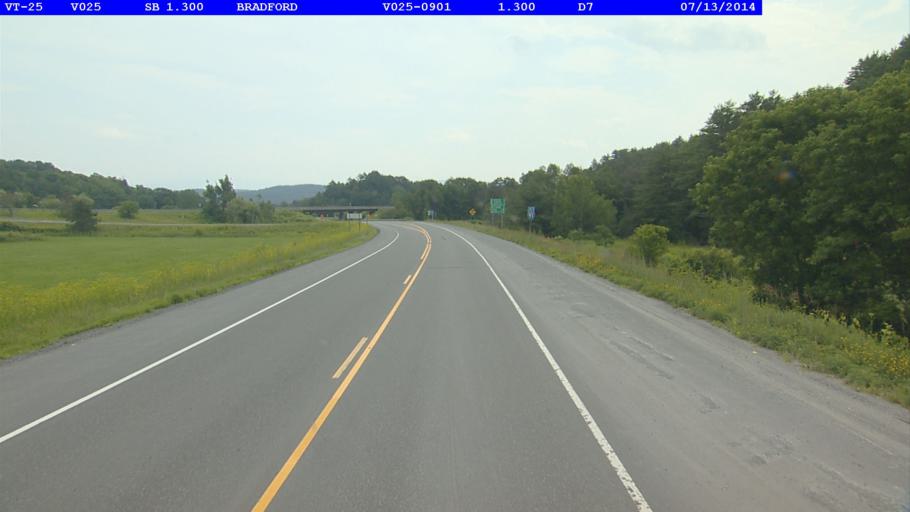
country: US
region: New Hampshire
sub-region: Grafton County
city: Orford
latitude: 43.9839
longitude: -72.1354
